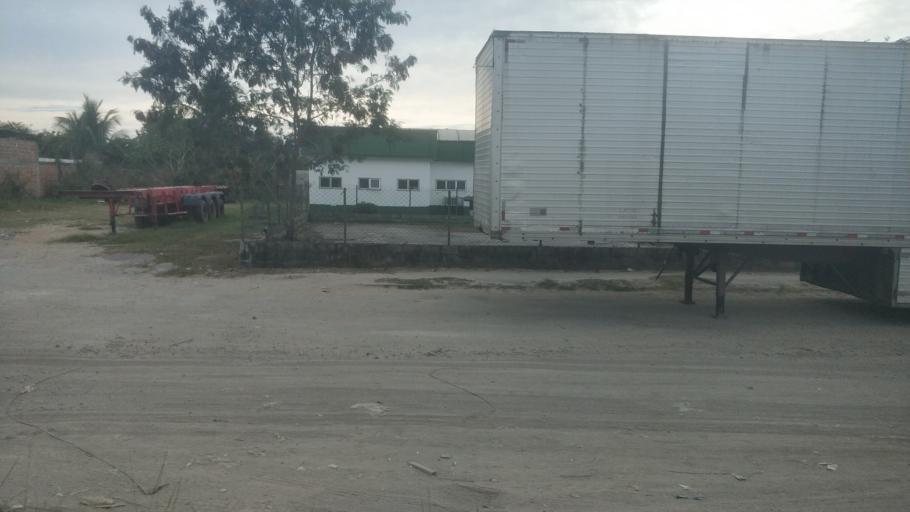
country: BR
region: Rio de Janeiro
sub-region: Seropedica
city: Seropedica
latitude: -22.8042
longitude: -43.6397
